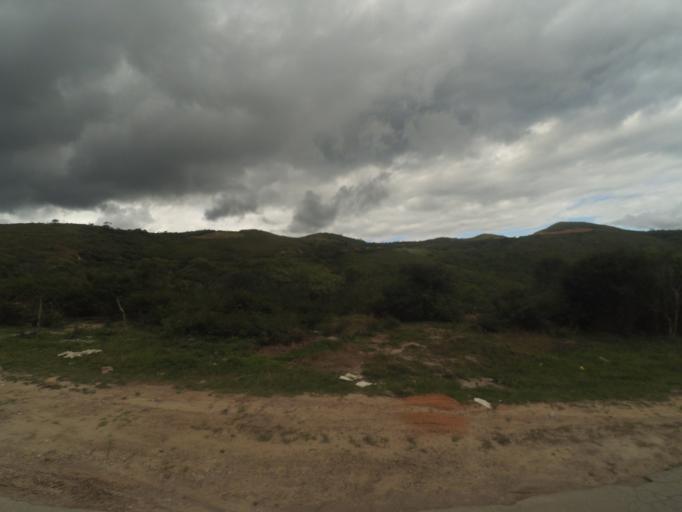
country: BO
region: Santa Cruz
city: Samaipata
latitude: -18.1745
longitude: -63.8747
